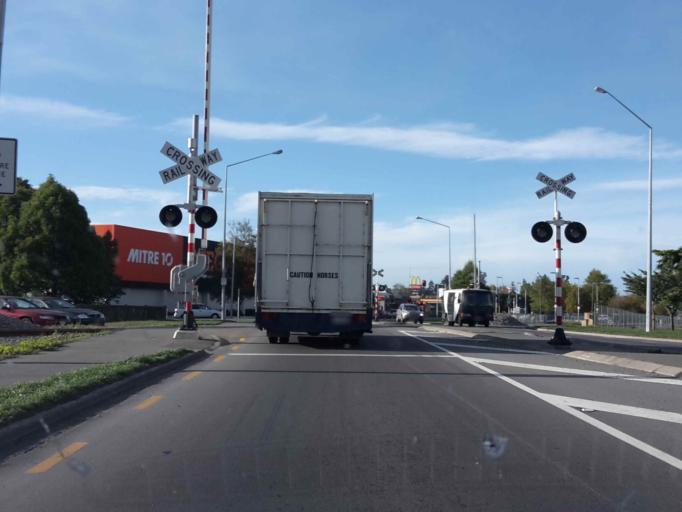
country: NZ
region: Canterbury
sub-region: Ashburton District
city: Ashburton
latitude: -43.9069
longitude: 171.7436
